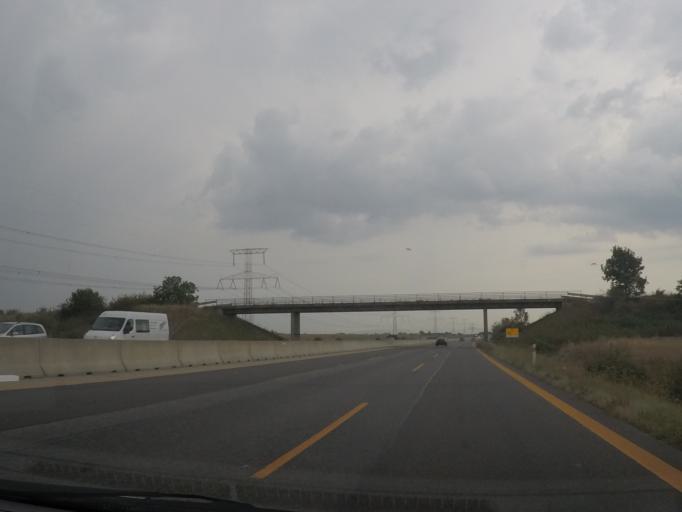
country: SK
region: Bratislavsky
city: Senec
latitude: 48.2149
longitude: 17.3145
